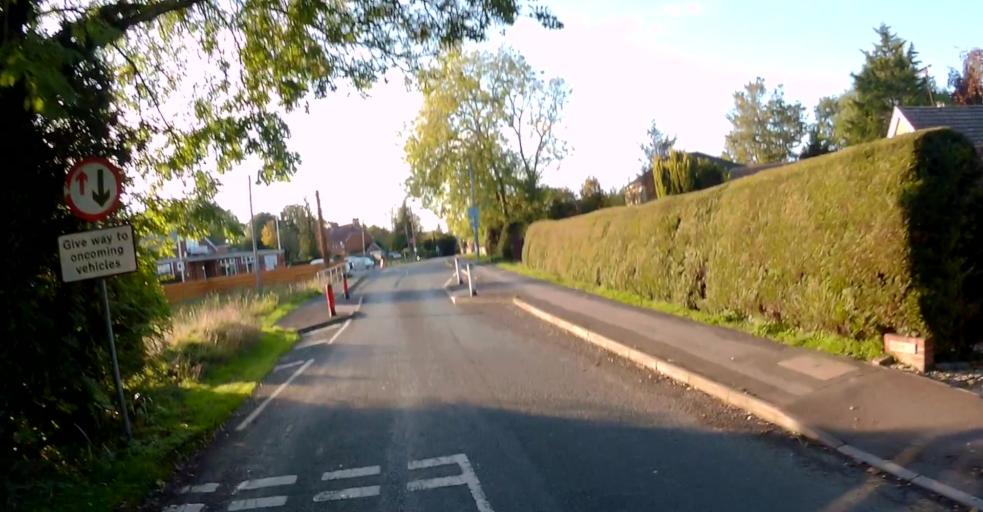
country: GB
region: England
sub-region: Hampshire
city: Old Basing
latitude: 51.2694
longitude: -1.0474
